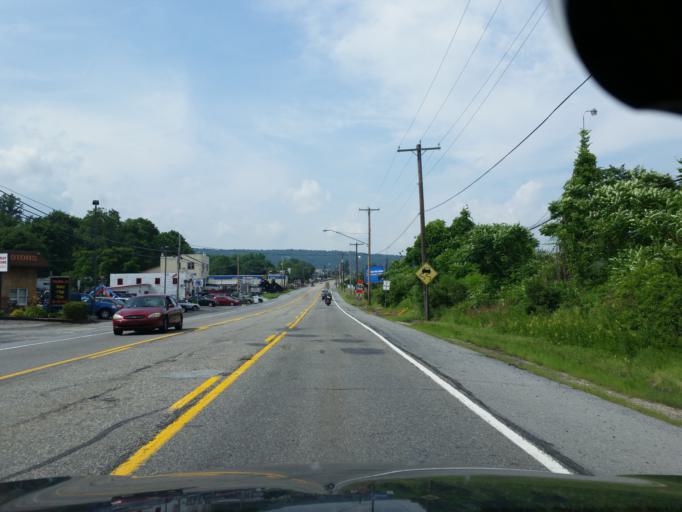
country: US
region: Pennsylvania
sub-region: Cumberland County
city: Enola
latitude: 40.2899
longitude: -76.9297
